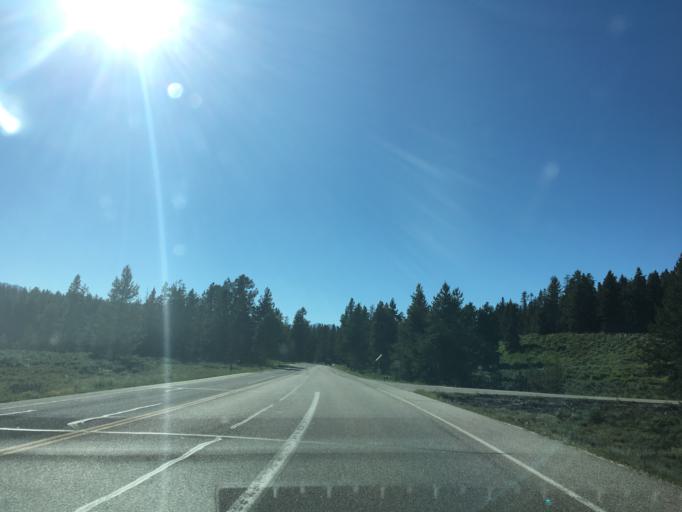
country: US
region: Wyoming
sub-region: Teton County
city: Jackson
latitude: 43.8448
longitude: -110.5134
